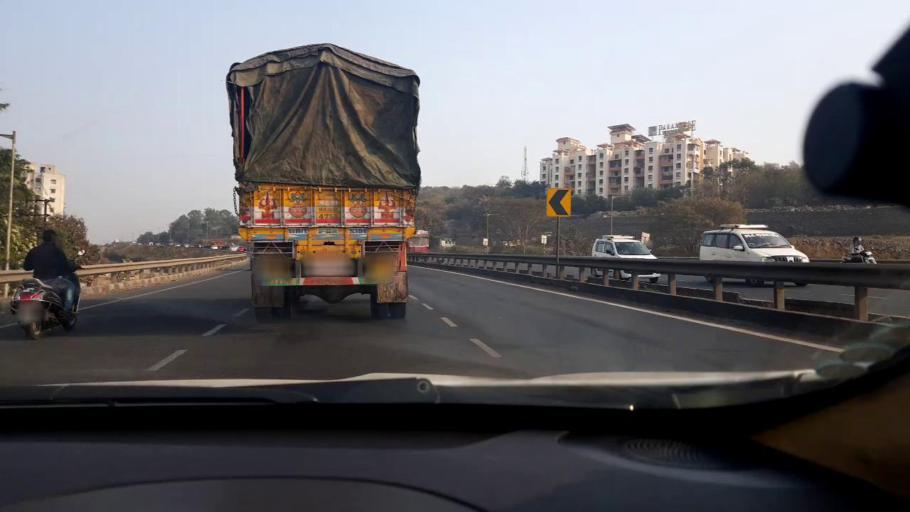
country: IN
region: Maharashtra
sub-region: Pune Division
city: Kharakvasla
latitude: 18.5099
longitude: 73.7735
